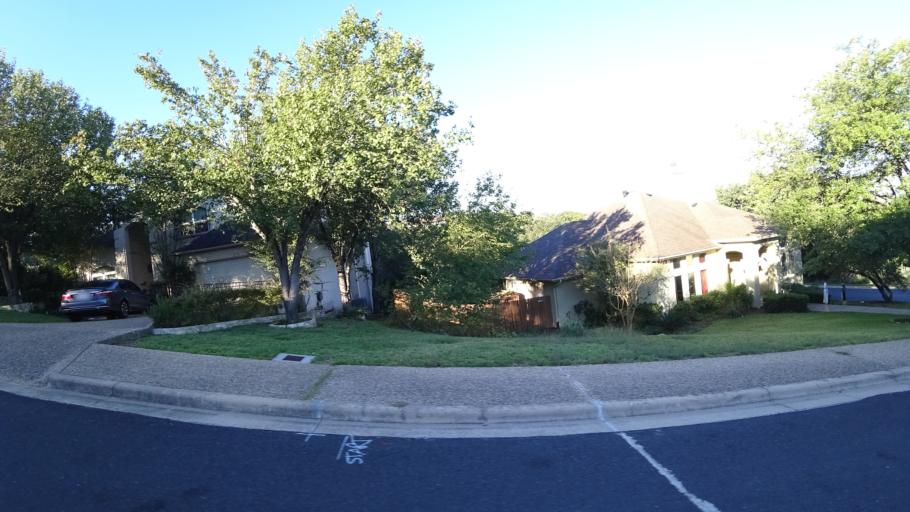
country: US
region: Texas
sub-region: Travis County
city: West Lake Hills
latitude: 30.3269
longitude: -97.8088
